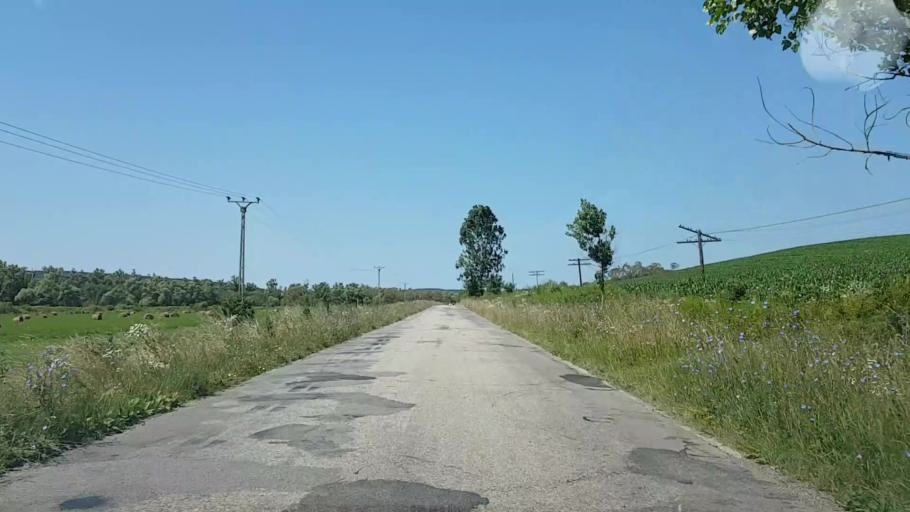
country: RO
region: Sibiu
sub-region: Comuna Iacobeni
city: Iacobeni
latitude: 46.0449
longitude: 24.7586
